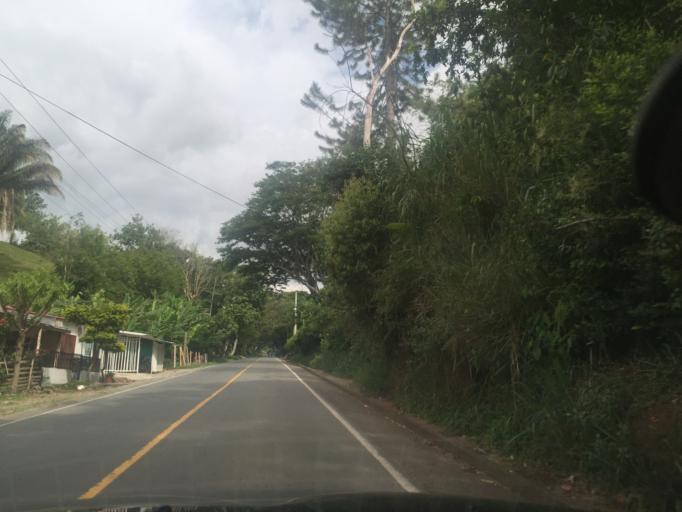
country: CO
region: Valle del Cauca
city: Caicedonia
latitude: 4.3413
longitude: -75.8407
